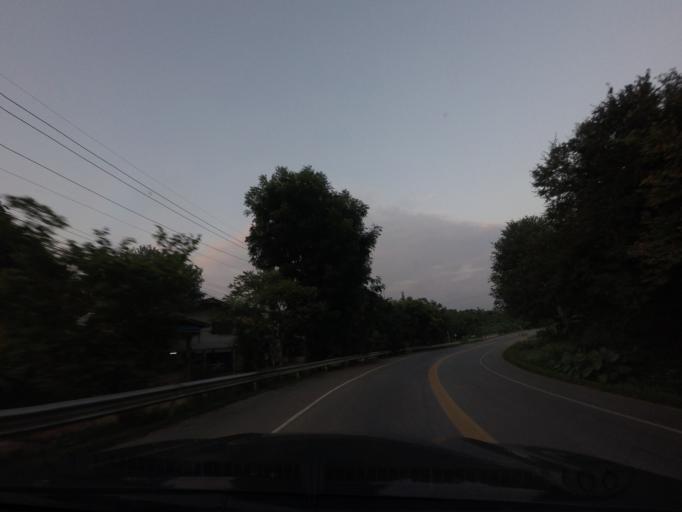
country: TH
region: Nan
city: Na Noi
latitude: 18.4546
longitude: 100.7121
